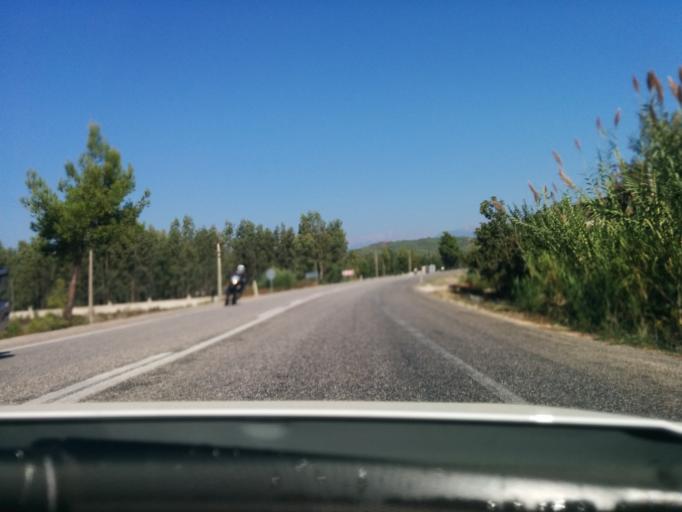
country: TR
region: Mugla
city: Kemer
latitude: 36.5845
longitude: 29.3504
